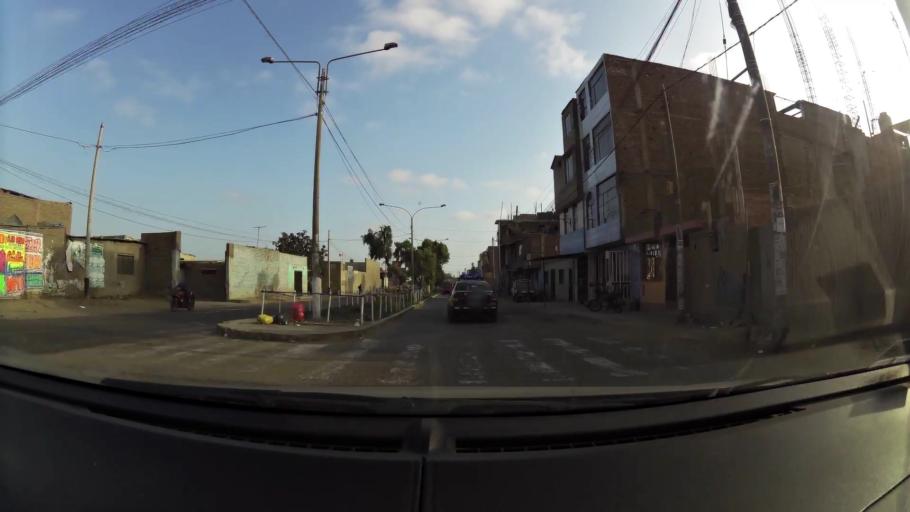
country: PE
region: La Libertad
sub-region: Provincia de Trujillo
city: El Porvenir
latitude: -8.0923
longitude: -79.0142
